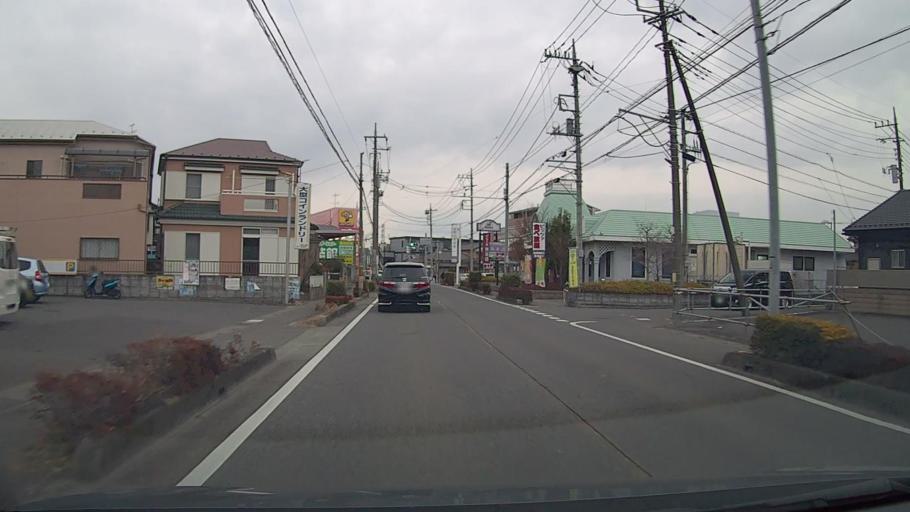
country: JP
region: Saitama
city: Wako
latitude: 35.8313
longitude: 139.6410
